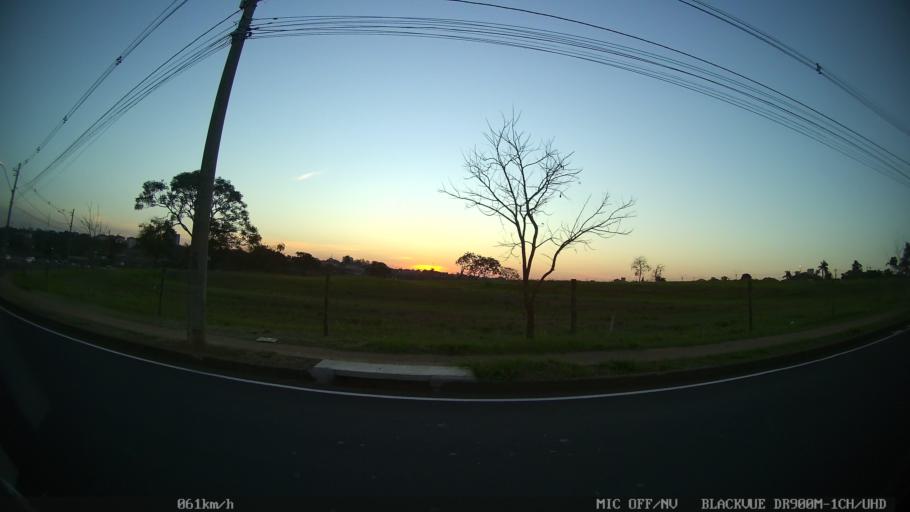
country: BR
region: Sao Paulo
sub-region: Sao Jose Do Rio Preto
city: Sao Jose do Rio Preto
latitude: -20.8240
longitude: -49.3415
